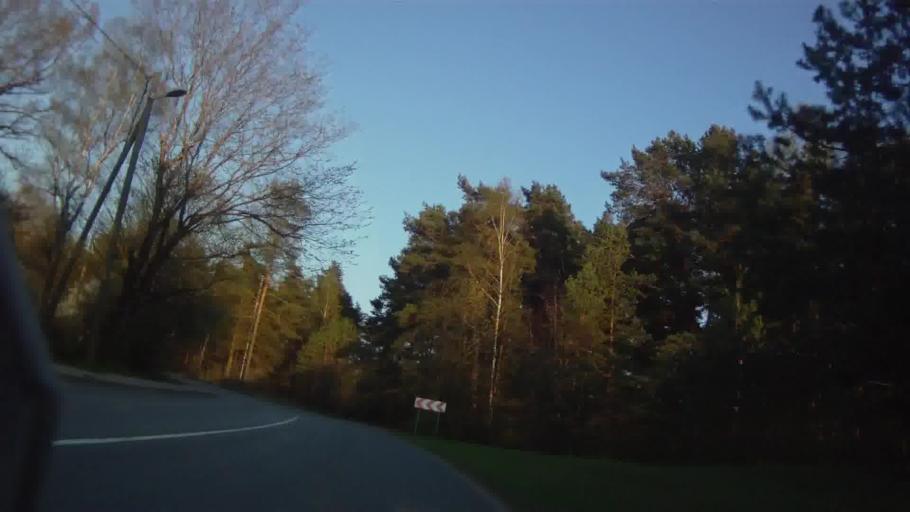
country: LV
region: Riga
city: Jaunciems
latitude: 57.0368
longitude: 24.1788
